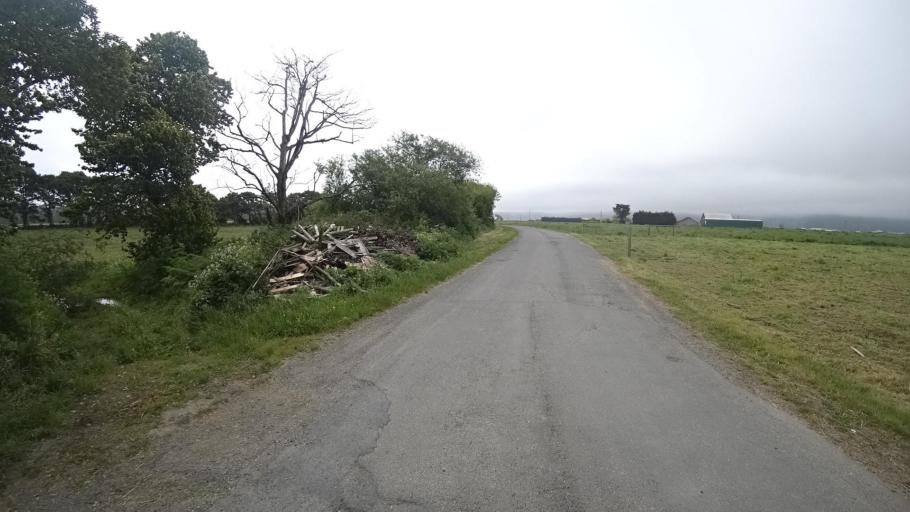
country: US
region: California
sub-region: Humboldt County
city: Fortuna
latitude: 40.5915
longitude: -124.1892
